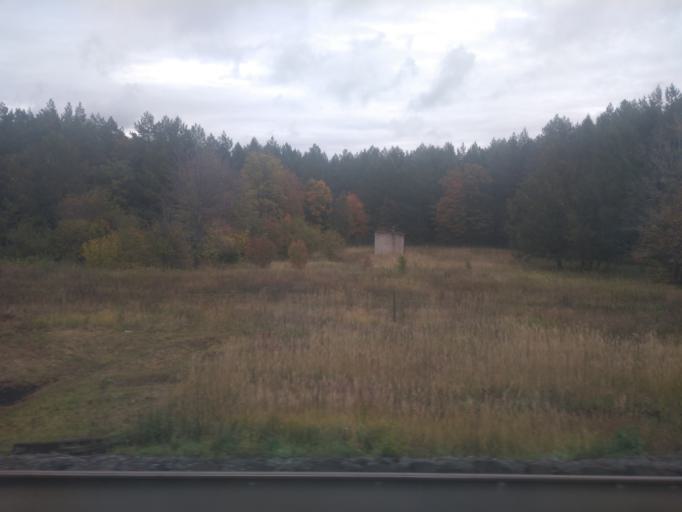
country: RU
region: Udmurtiya
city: Alnashi
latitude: 56.1167
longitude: 52.5641
